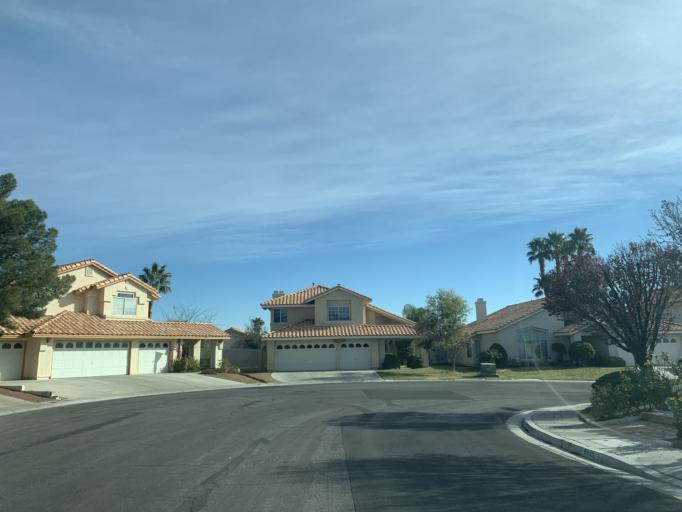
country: US
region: Nevada
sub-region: Clark County
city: Spring Valley
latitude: 36.1291
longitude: -115.2846
